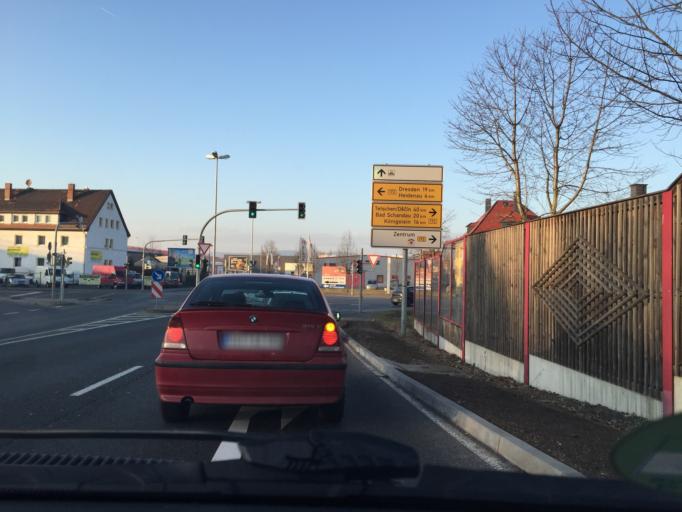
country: DE
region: Saxony
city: Pirna
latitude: 50.9568
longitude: 13.9193
